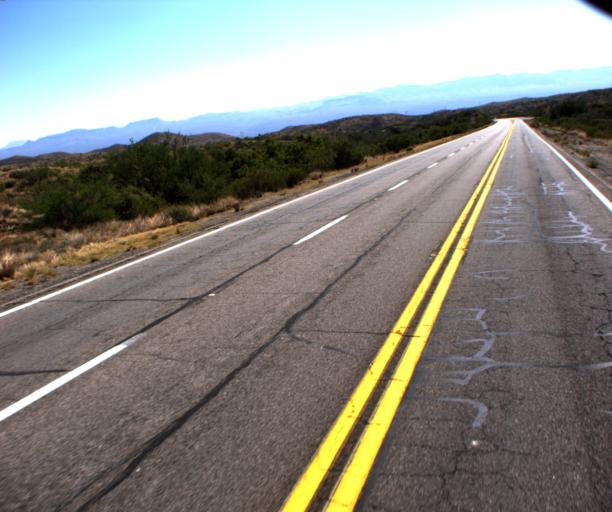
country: US
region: Arizona
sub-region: Pinal County
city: Oracle
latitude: 32.6241
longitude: -110.7544
